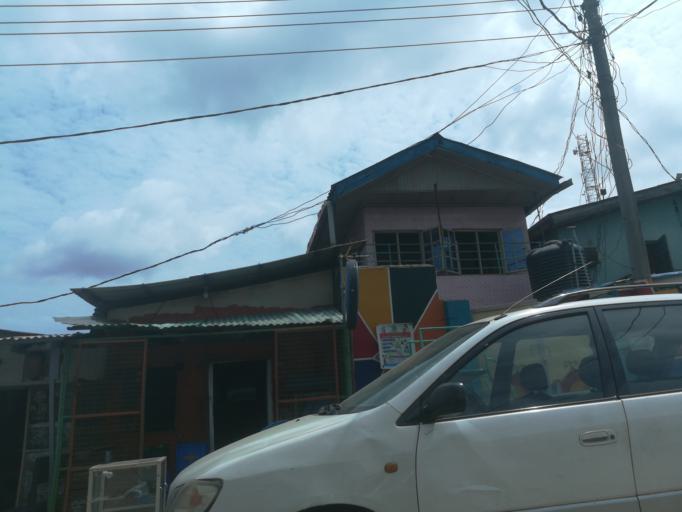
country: NG
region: Lagos
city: Somolu
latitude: 6.5247
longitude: 3.3826
